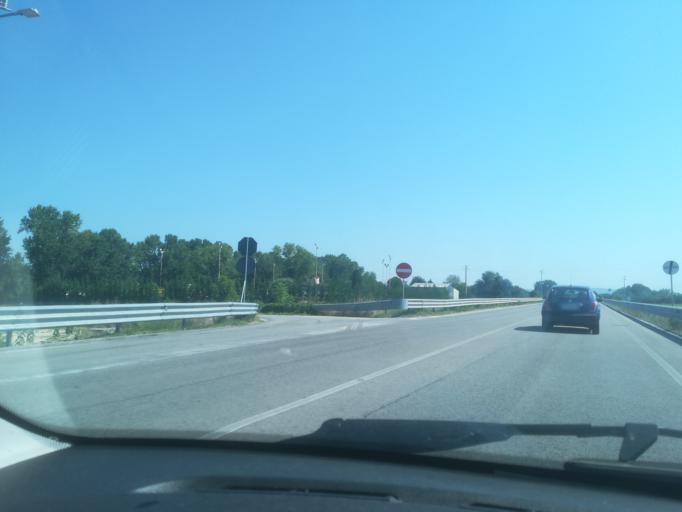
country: IT
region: The Marches
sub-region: Provincia di Macerata
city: Villa Potenza
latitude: 43.3279
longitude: 13.4302
